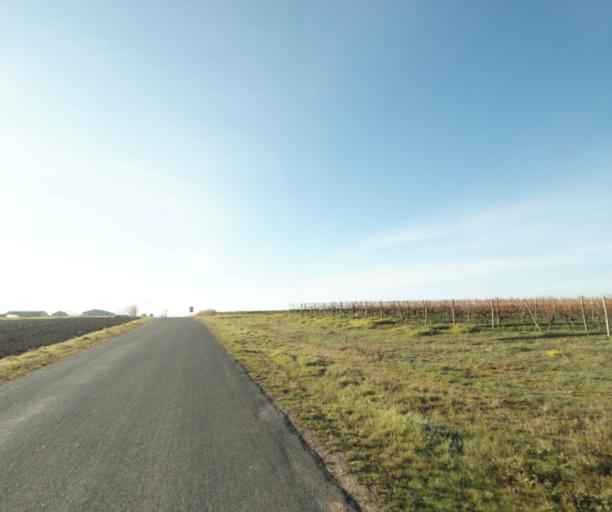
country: FR
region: Poitou-Charentes
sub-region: Departement de la Charente-Maritime
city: Cherac
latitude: 45.6928
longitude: -0.4496
